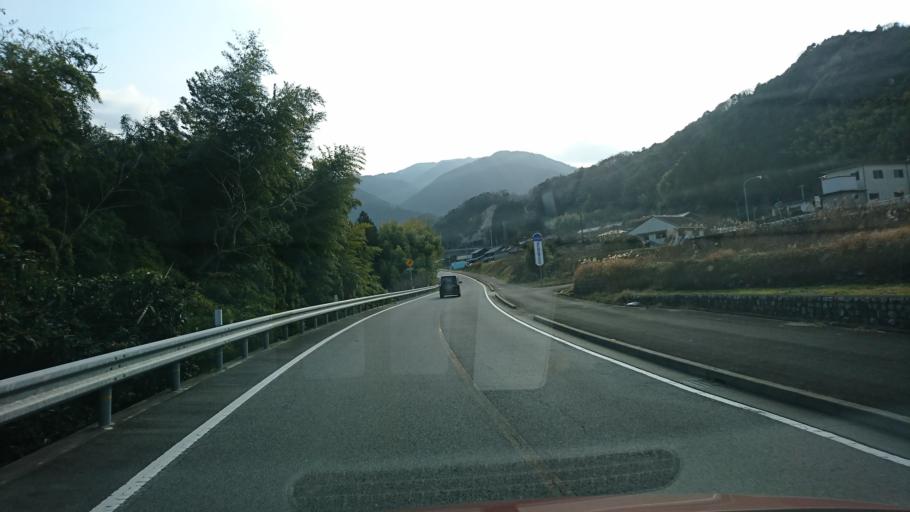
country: JP
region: Ehime
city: Hojo
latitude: 33.9780
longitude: 132.9049
